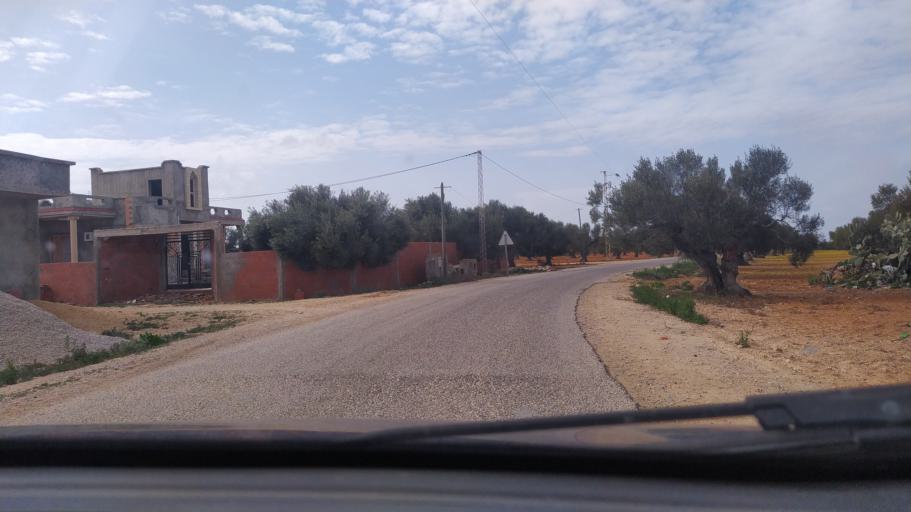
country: TN
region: Al Munastir
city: Sidi Bin Nur
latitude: 35.5271
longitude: 10.9648
